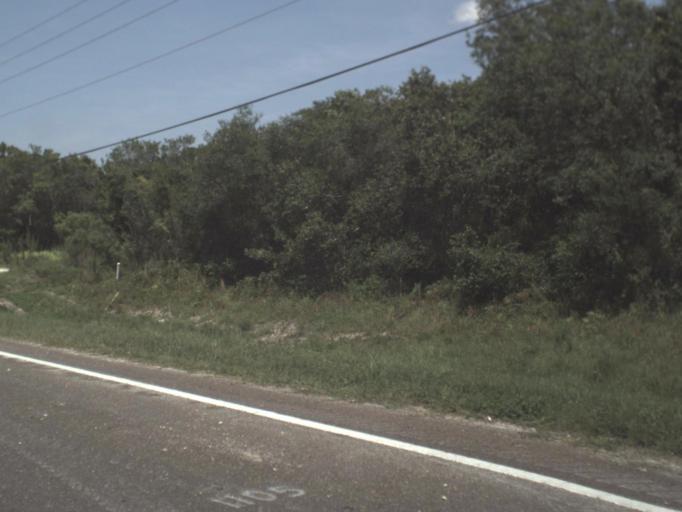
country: US
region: Florida
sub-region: Hernando County
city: Hernando Beach
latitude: 28.4230
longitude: -82.6450
